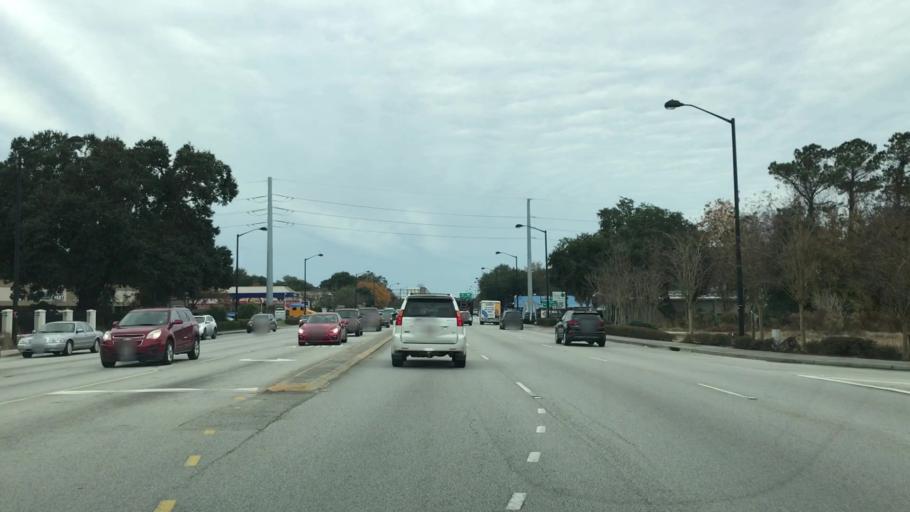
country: US
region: South Carolina
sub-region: Charleston County
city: Mount Pleasant
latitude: 32.8193
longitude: -79.8437
